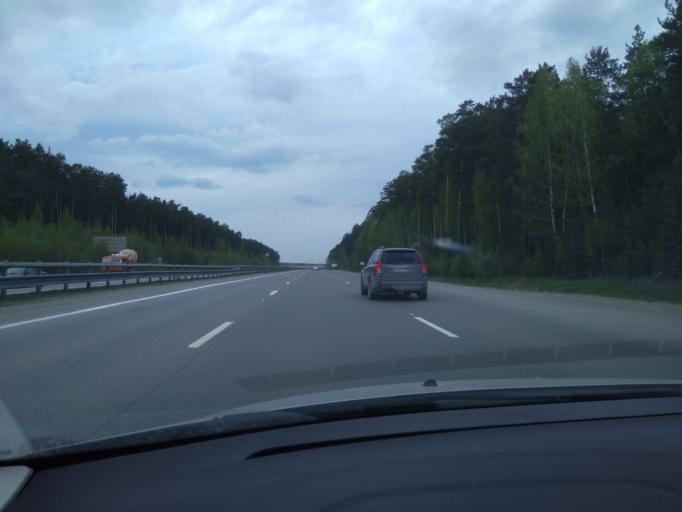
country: RU
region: Sverdlovsk
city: Shuvakish
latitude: 56.8889
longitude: 60.5464
